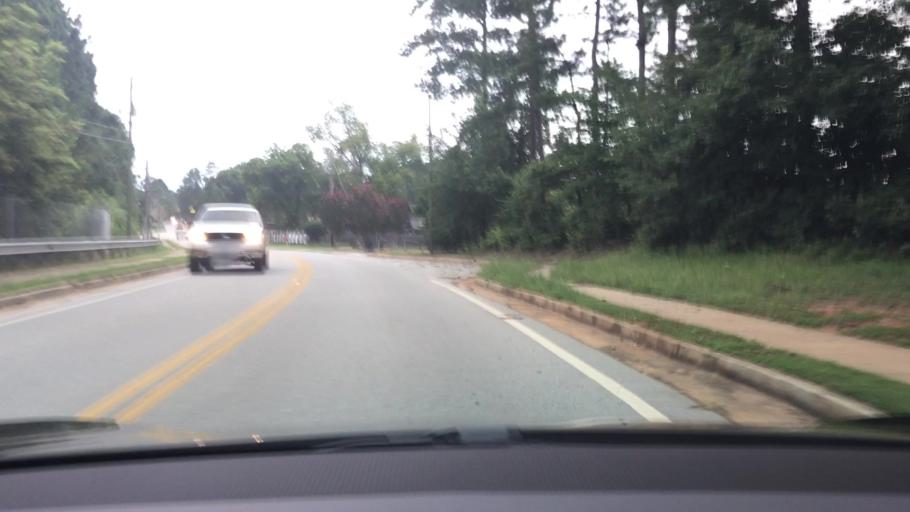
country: US
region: Georgia
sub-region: Gwinnett County
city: Suwanee
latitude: 34.0865
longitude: -84.0679
